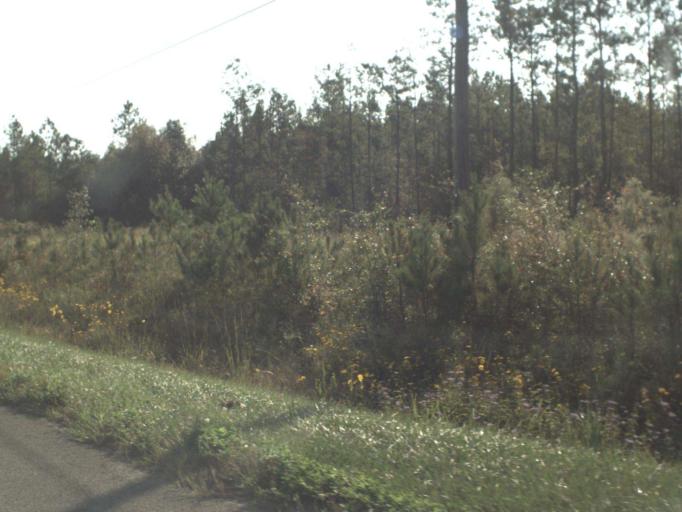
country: US
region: Florida
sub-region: Holmes County
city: Bonifay
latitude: 30.5973
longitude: -85.7730
